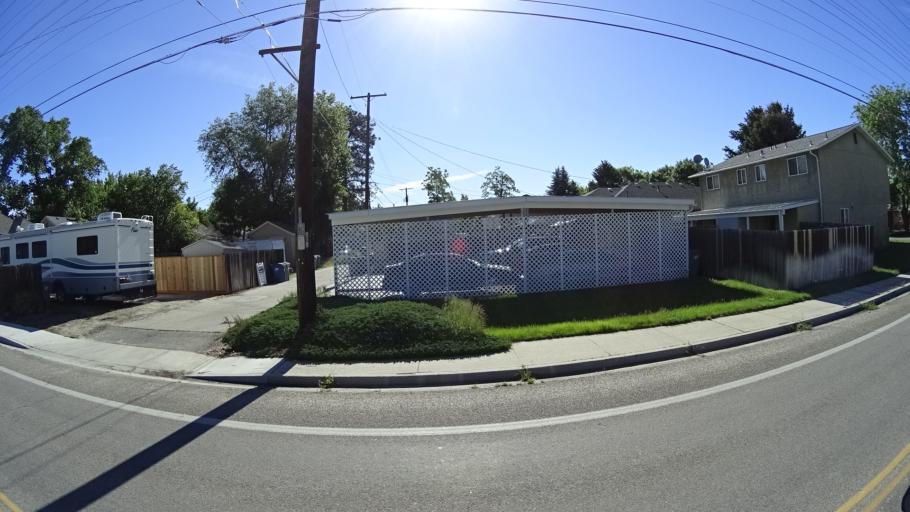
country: US
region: Idaho
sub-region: Ada County
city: Garden City
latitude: 43.6277
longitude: -116.2240
